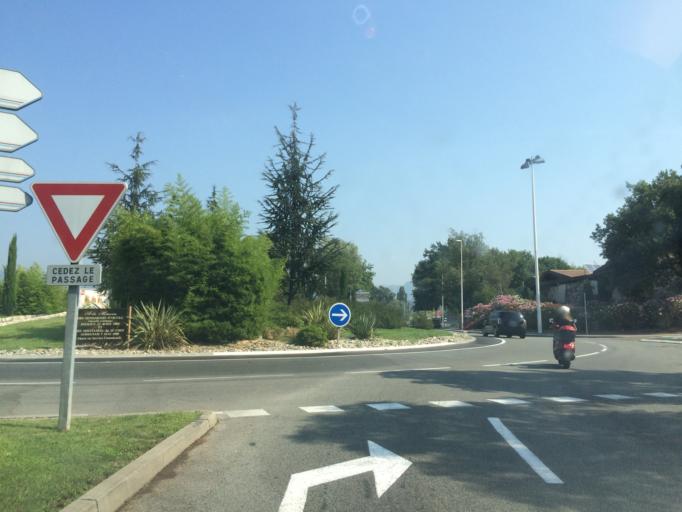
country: FR
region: Provence-Alpes-Cote d'Azur
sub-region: Departement des Alpes-Maritimes
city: Villeneuve-Loubet
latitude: 43.6698
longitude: 7.1256
